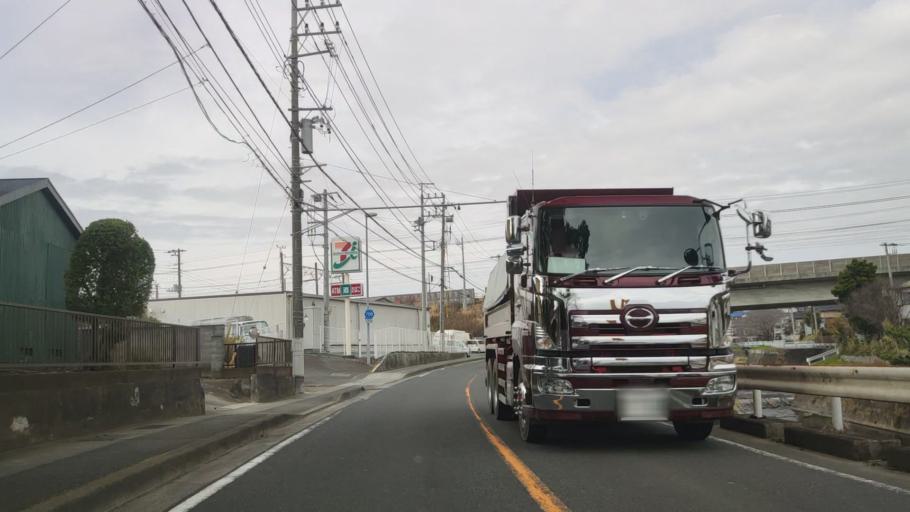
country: JP
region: Kanagawa
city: Ninomiya
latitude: 35.2904
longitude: 139.2362
